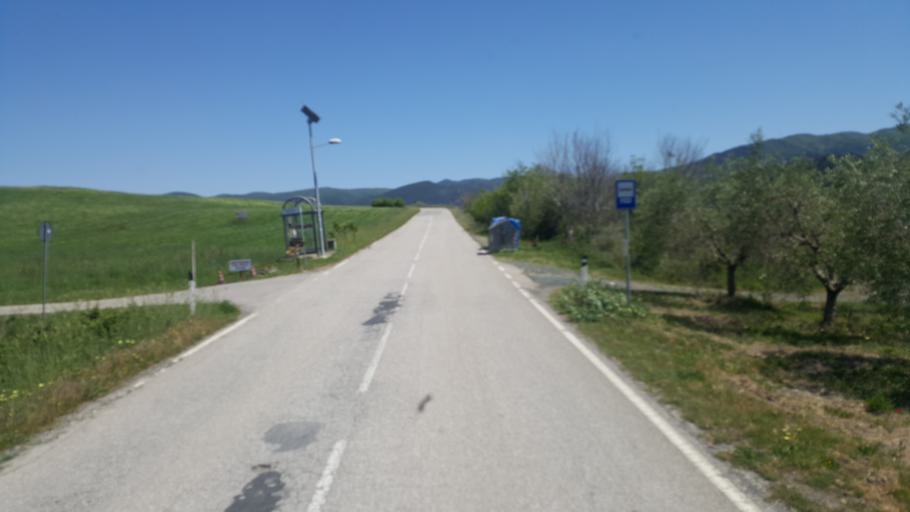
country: IT
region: Tuscany
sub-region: Provincia di Livorno
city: Rosignano Marittimo
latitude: 43.4164
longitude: 10.5194
